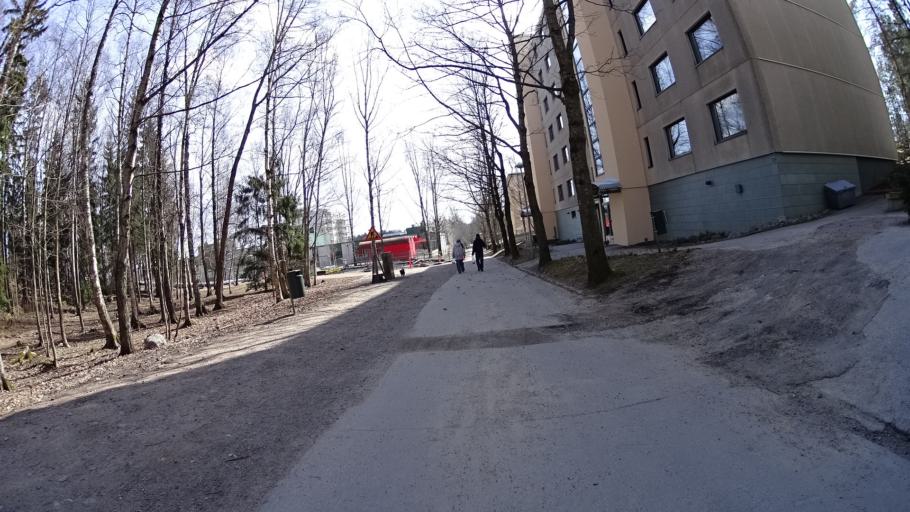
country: FI
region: Uusimaa
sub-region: Helsinki
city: Kilo
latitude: 60.2774
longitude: 24.8414
